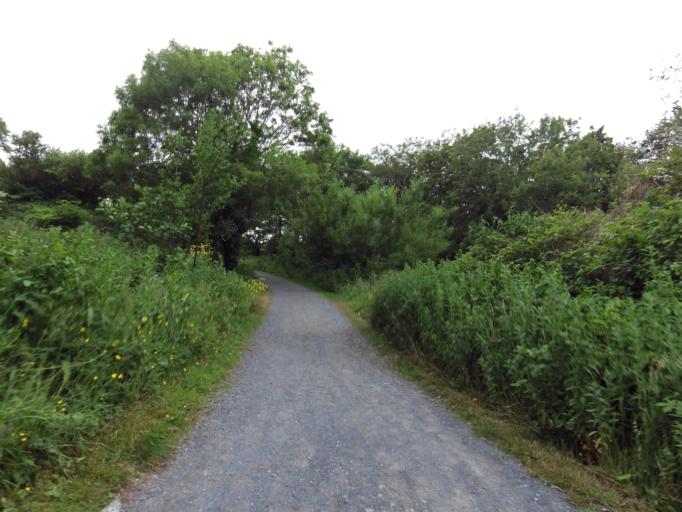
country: IE
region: Connaught
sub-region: County Galway
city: Gaillimh
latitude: 53.2941
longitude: -9.0796
